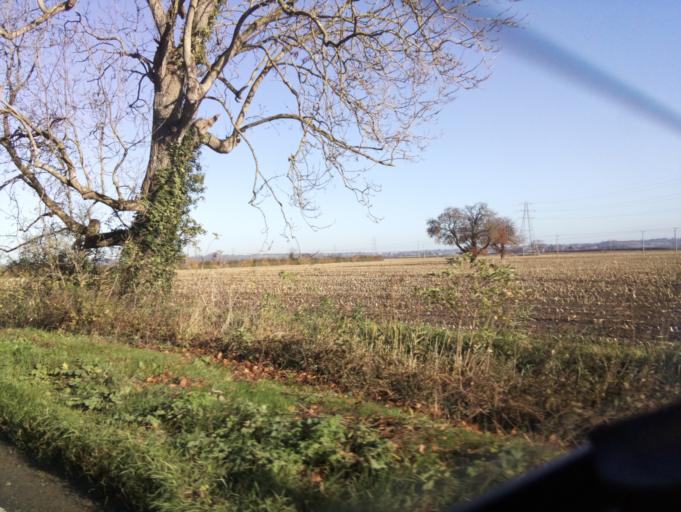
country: GB
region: England
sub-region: Somerset
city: Bridgwater
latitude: 51.1206
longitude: -2.9660
